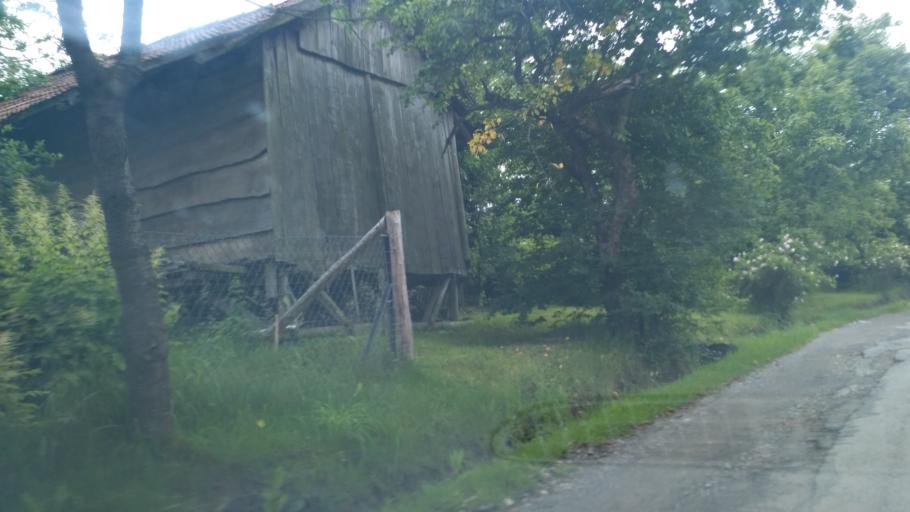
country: PL
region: Subcarpathian Voivodeship
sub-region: Powiat jaroslawski
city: Pruchnik
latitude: 49.8866
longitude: 22.5202
